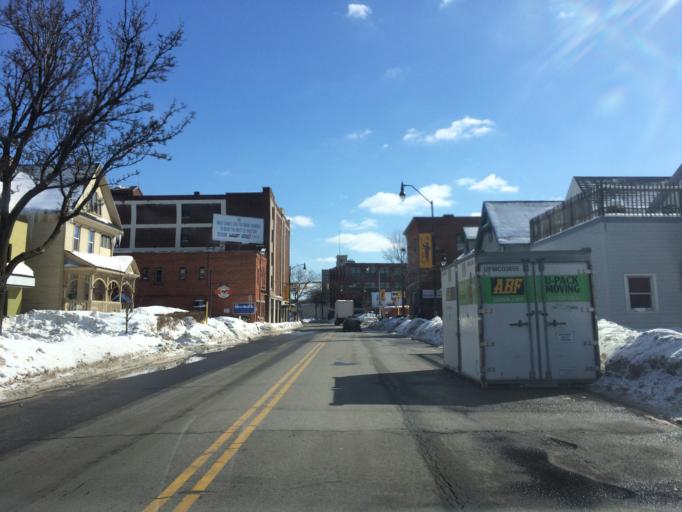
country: US
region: New York
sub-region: Monroe County
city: Rochester
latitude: 43.1443
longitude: -77.6008
